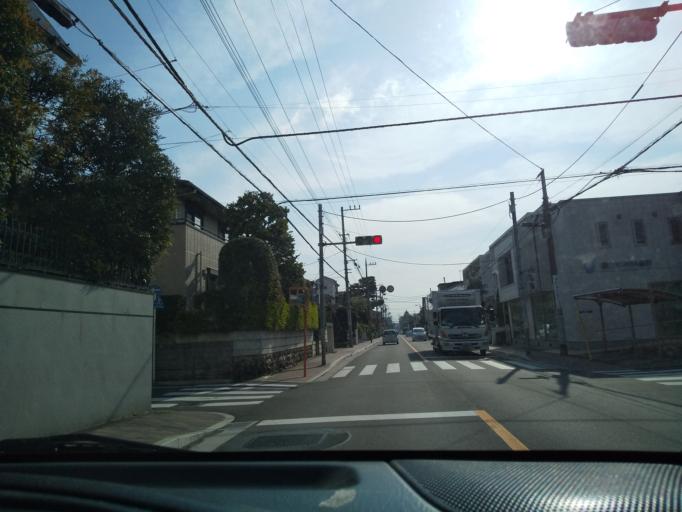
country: JP
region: Tokyo
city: Kokubunji
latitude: 35.6904
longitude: 139.4388
